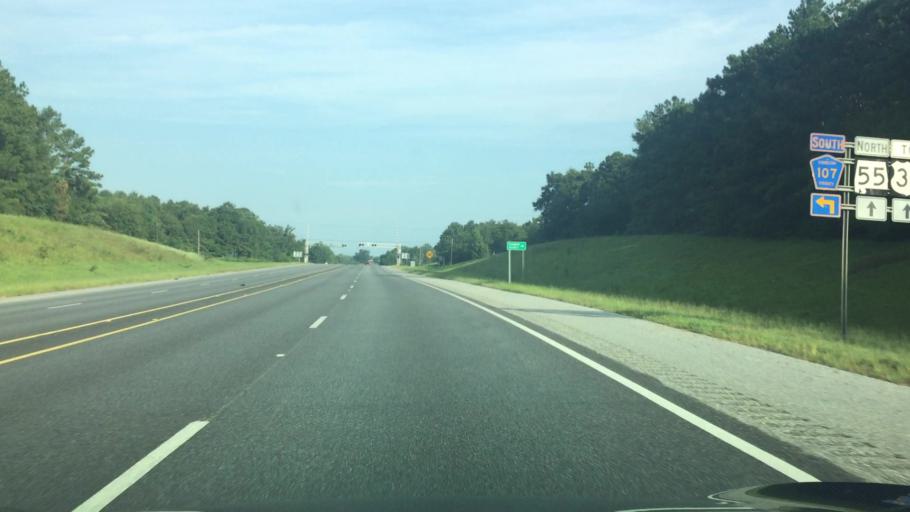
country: US
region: Alabama
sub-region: Butler County
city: Georgiana
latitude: 31.5152
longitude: -86.7043
